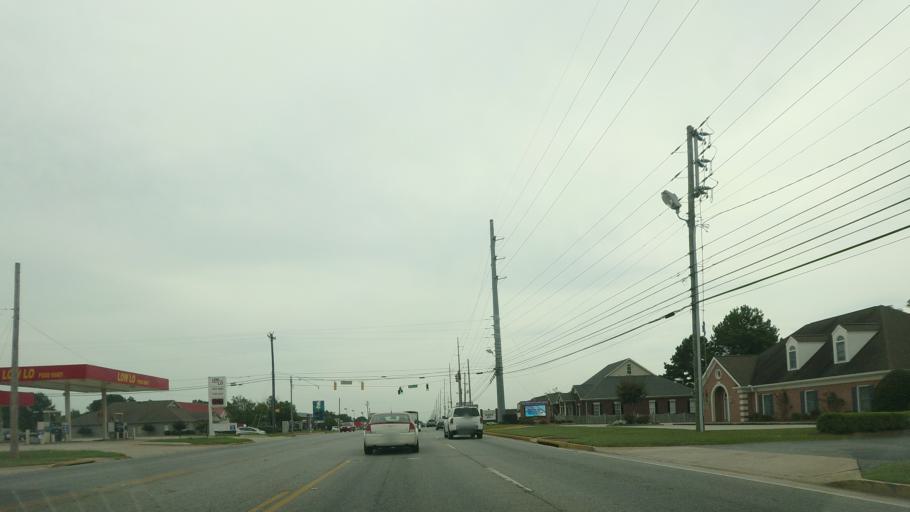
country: US
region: Georgia
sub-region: Houston County
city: Centerville
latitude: 32.5939
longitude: -83.6519
